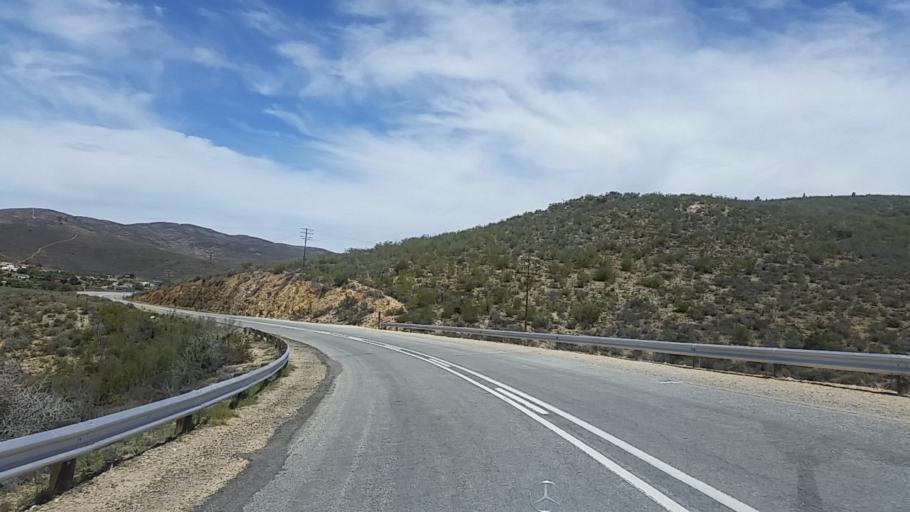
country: ZA
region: Western Cape
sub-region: Eden District Municipality
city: Knysna
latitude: -33.6427
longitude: 23.1333
